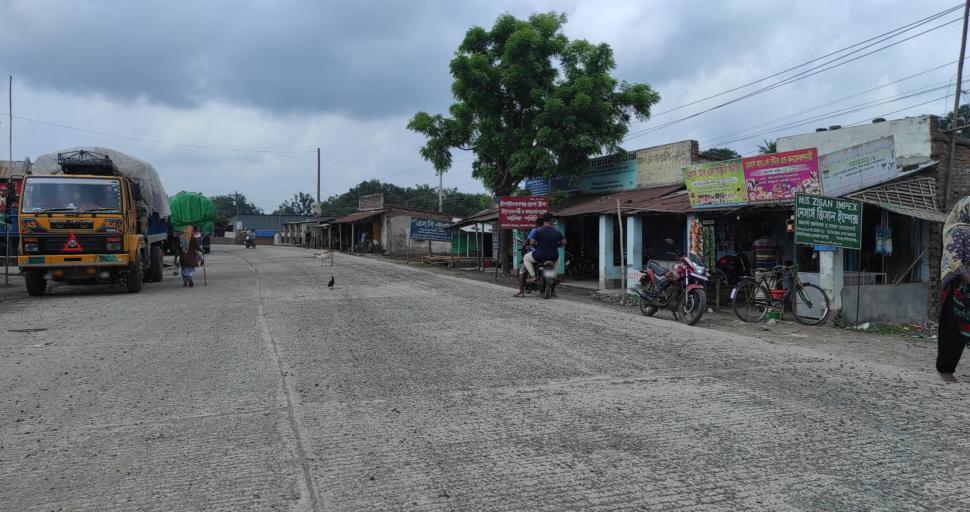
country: BD
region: Rajshahi
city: Shibganj
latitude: 24.8351
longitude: 88.1416
